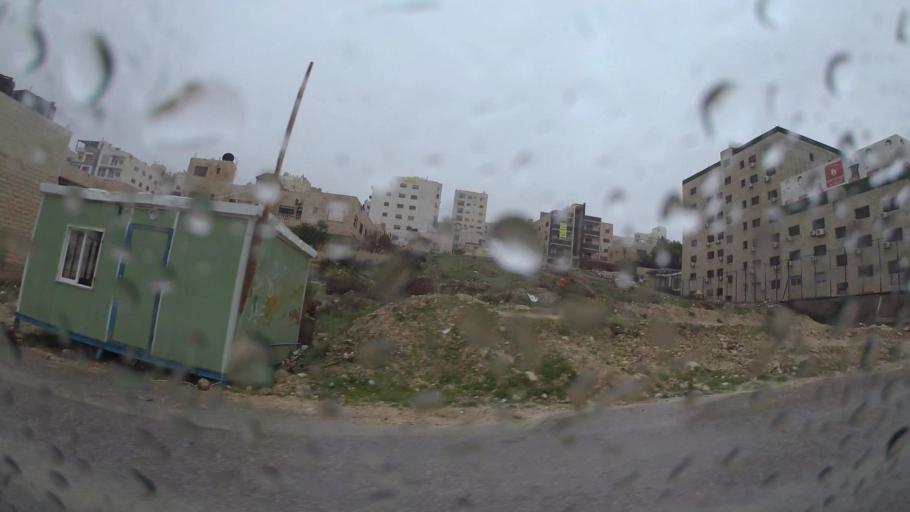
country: JO
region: Amman
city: Al Jubayhah
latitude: 32.0117
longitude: 35.8936
